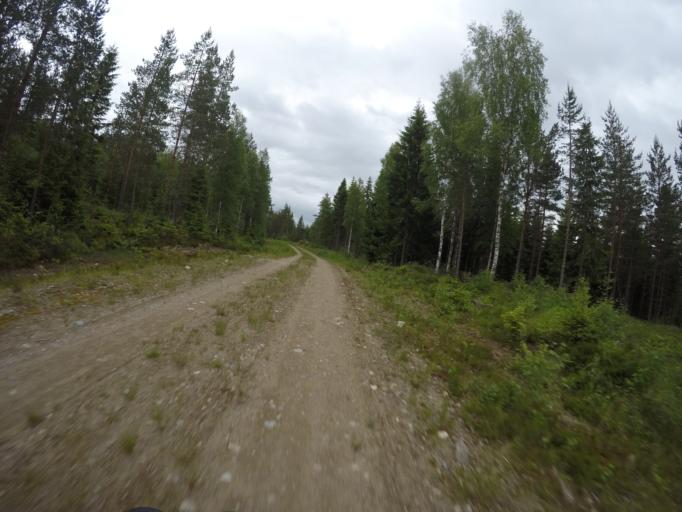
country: SE
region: Dalarna
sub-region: Ludvika Kommun
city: Abborrberget
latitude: 60.0640
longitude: 14.5597
